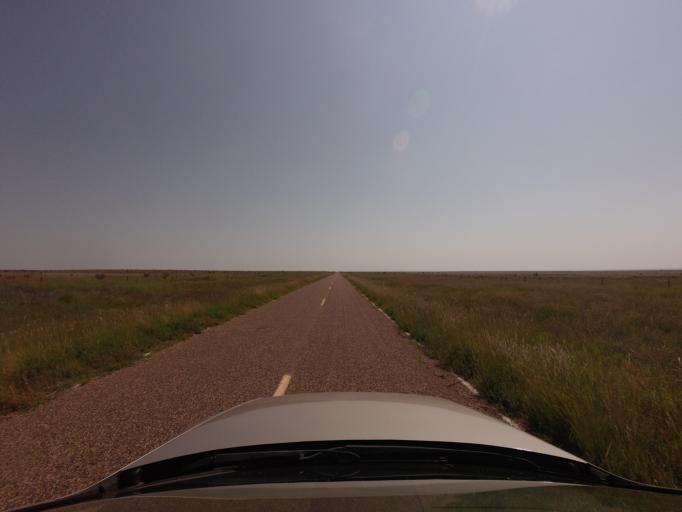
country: US
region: New Mexico
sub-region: Curry County
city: Cannon Air Force Base
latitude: 34.6331
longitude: -103.4166
